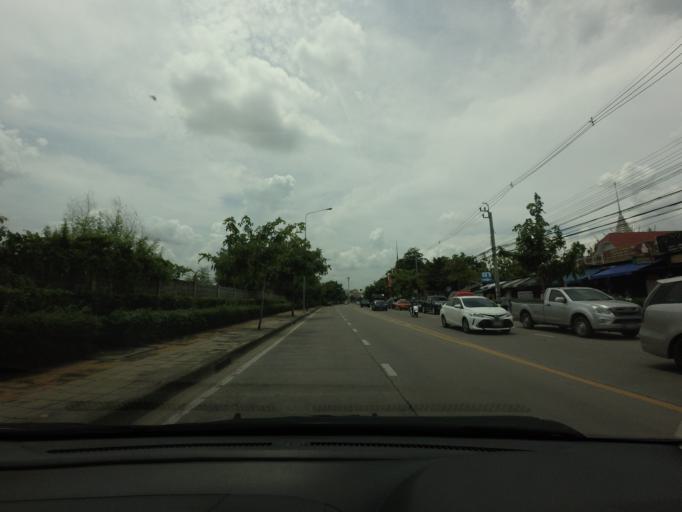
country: TH
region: Bangkok
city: Don Mueang
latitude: 13.9470
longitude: 100.5742
